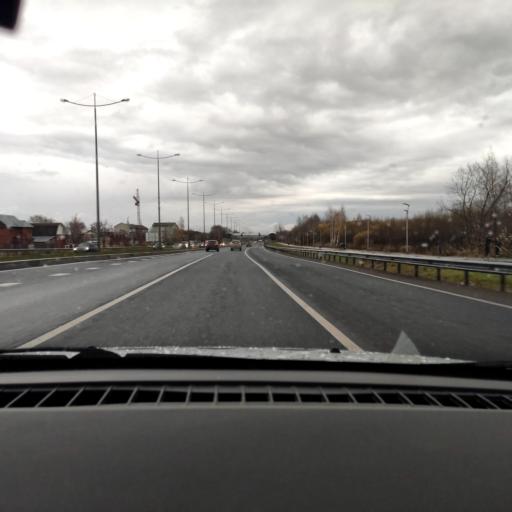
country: RU
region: Perm
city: Kondratovo
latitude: 57.9397
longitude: 56.0554
